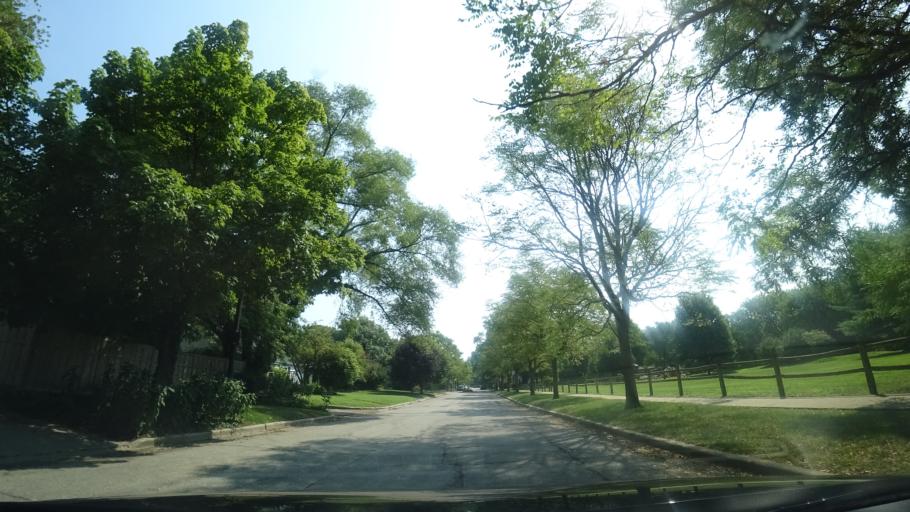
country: US
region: Illinois
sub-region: Cook County
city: Evanston
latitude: 42.0231
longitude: -87.6929
